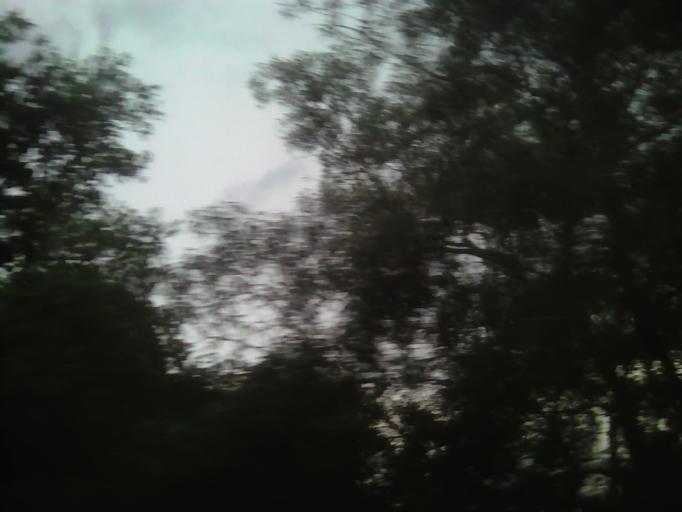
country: MY
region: Penang
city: Perai
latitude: 5.4057
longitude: 100.3876
